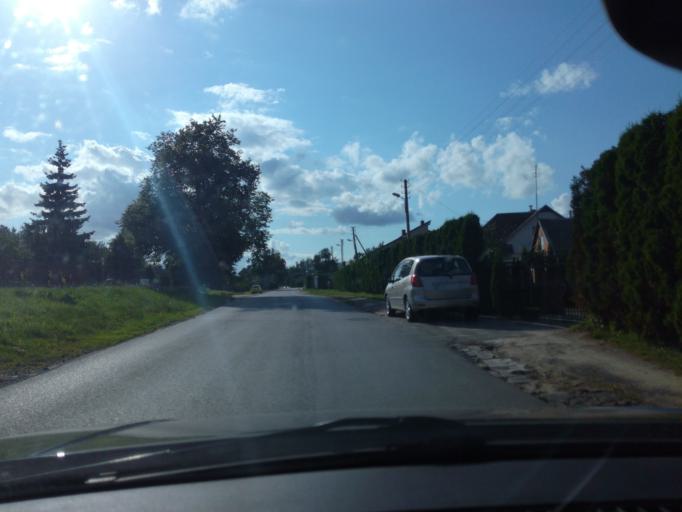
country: LT
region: Alytaus apskritis
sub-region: Alytus
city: Alytus
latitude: 54.4083
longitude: 24.0151
